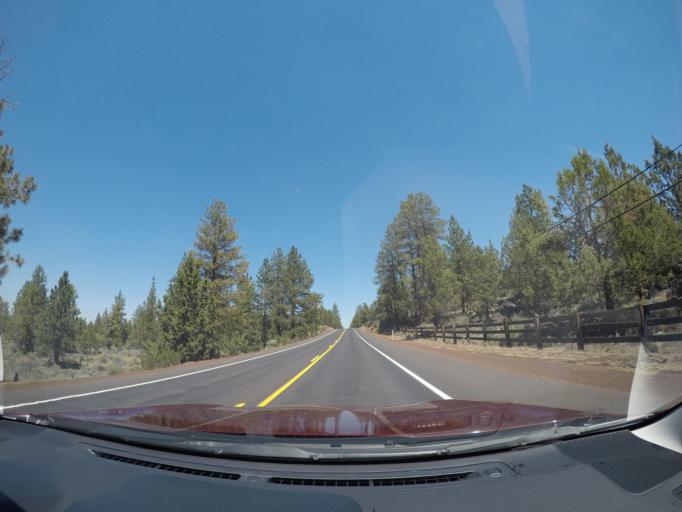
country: US
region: Oregon
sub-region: Deschutes County
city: Sisters
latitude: 44.2877
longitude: -121.5080
